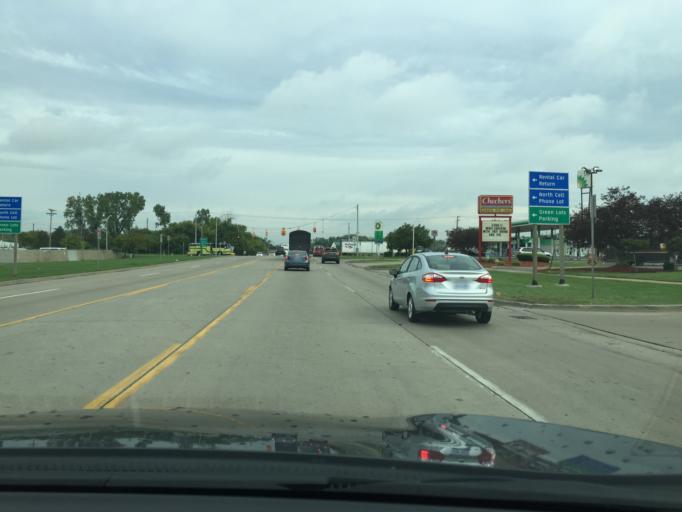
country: US
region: Michigan
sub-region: Wayne County
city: Taylor
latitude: 42.2377
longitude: -83.3277
